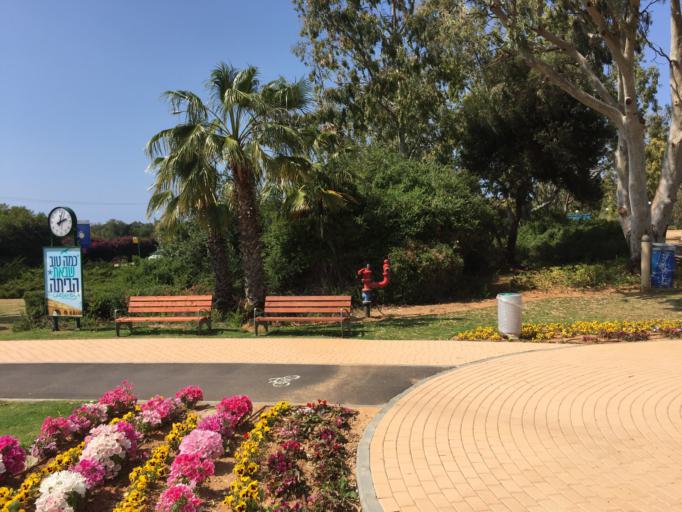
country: IL
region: Haifa
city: Qesarya
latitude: 32.5035
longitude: 34.9052
